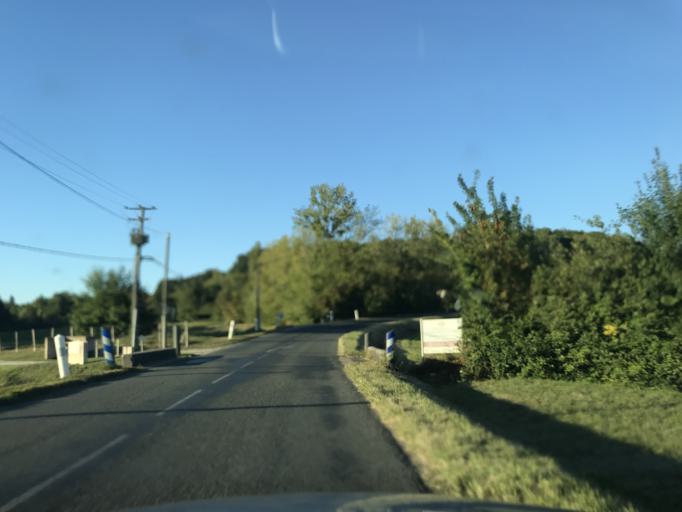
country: FR
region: Aquitaine
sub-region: Departement de la Gironde
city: Mouliets-et-Villemartin
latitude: 44.8753
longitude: -0.0478
